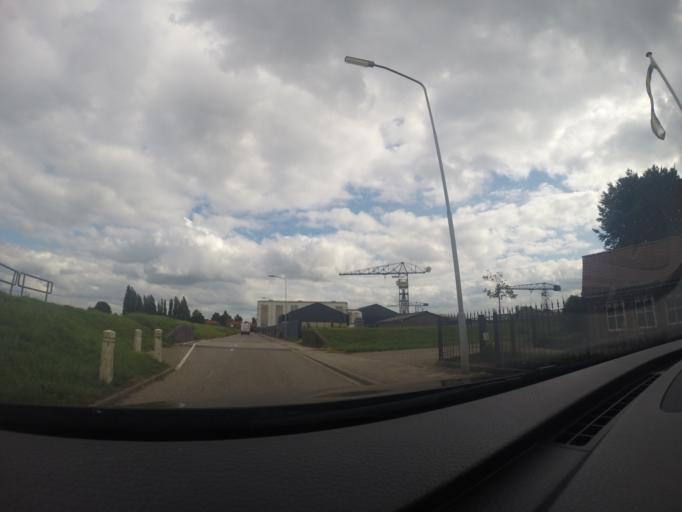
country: NL
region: Gelderland
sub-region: Gemeente Zevenaar
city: Zevenaar
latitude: 51.8555
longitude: 6.0956
